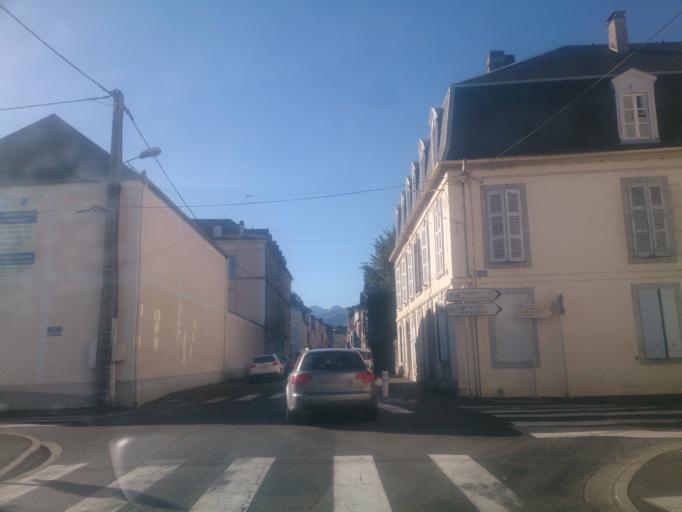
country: FR
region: Midi-Pyrenees
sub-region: Departement des Hautes-Pyrenees
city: Bagneres-de-Bigorre
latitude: 43.0677
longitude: 0.1472
